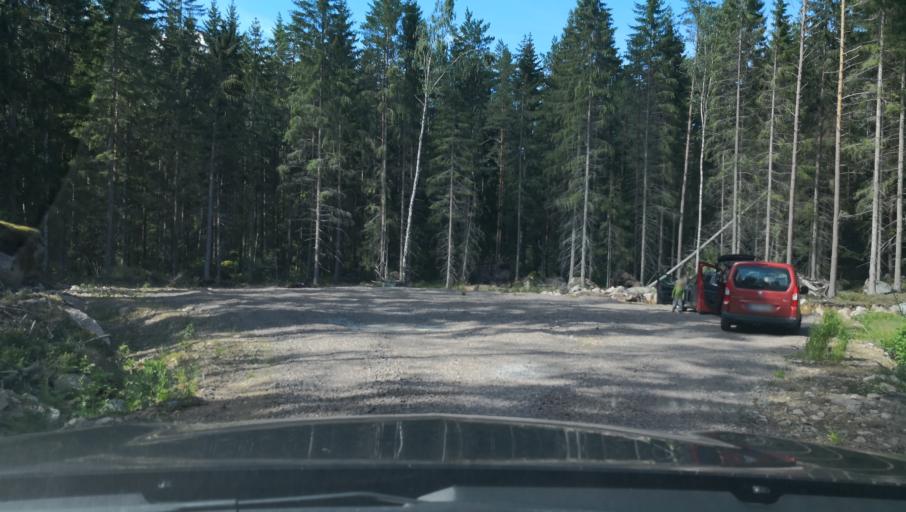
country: SE
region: Vaestmanland
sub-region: Hallstahammars Kommun
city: Hallstahammar
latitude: 59.6581
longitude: 16.2015
